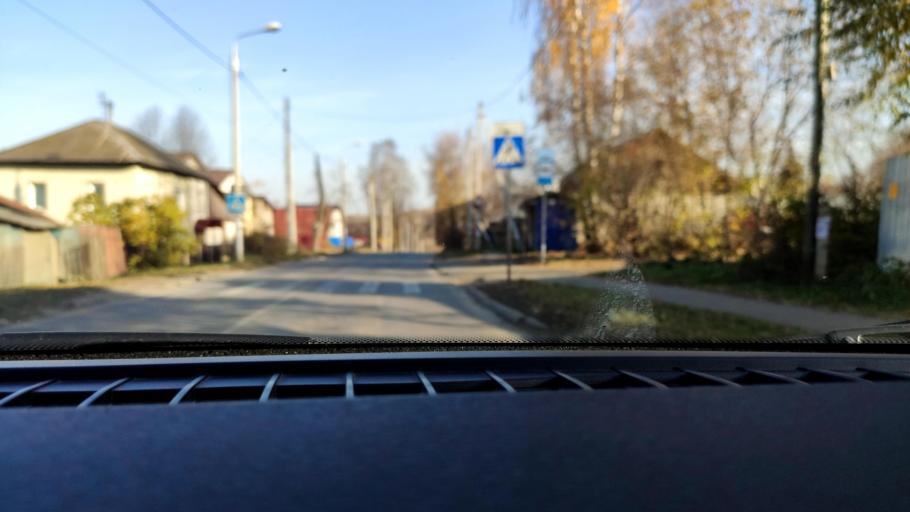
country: RU
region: Perm
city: Perm
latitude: 58.0240
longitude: 56.3126
